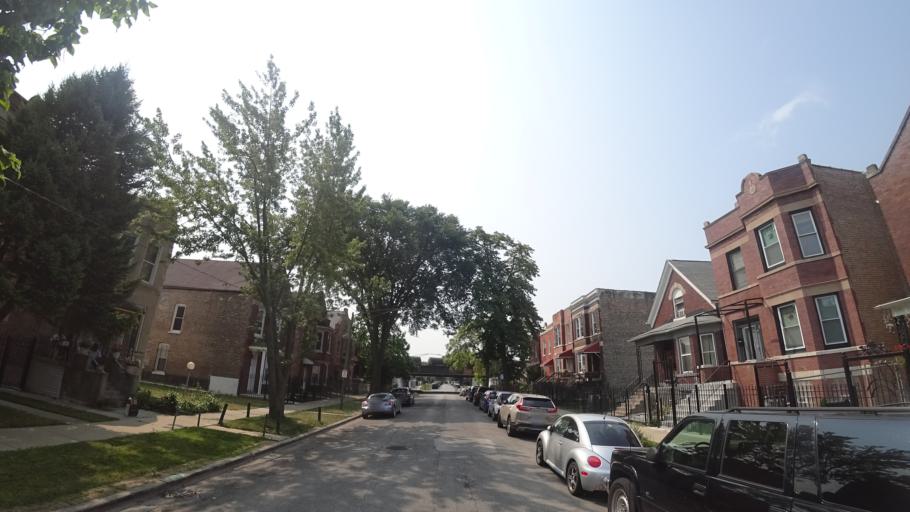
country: US
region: Illinois
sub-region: Cook County
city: Cicero
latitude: 41.8508
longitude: -87.7198
